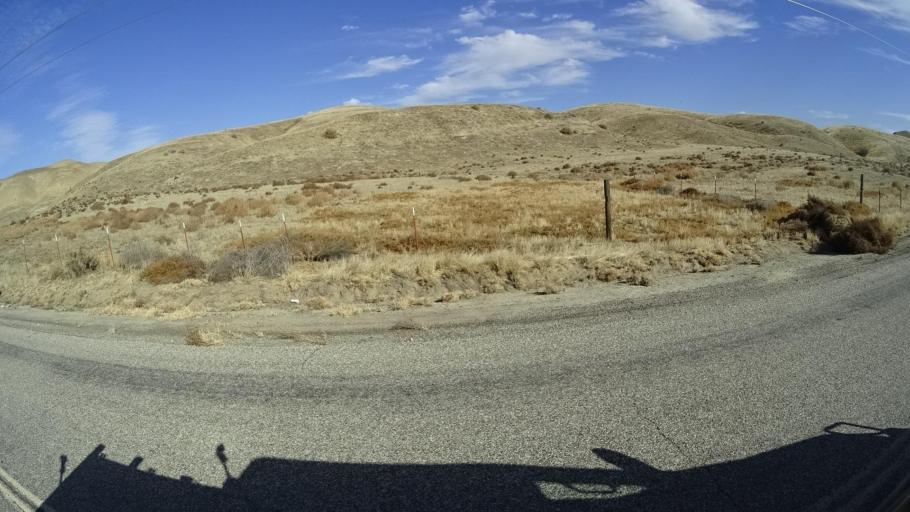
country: US
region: California
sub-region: Kern County
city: Oildale
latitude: 35.5273
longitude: -118.9506
